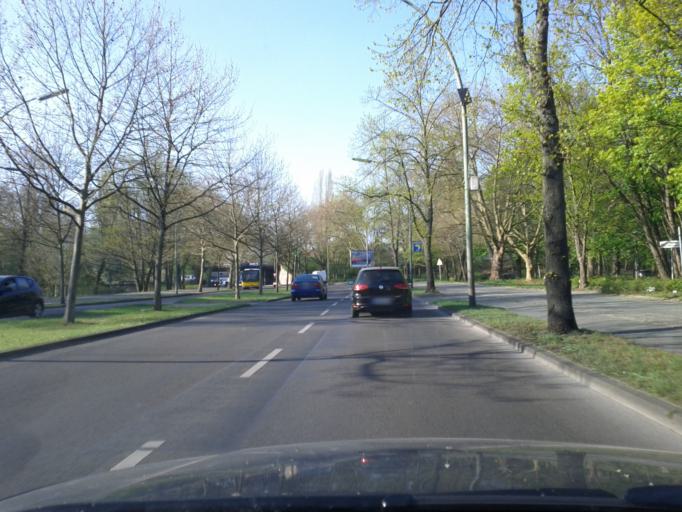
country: DE
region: Berlin
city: Reinickendorf
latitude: 52.5767
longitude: 13.3480
